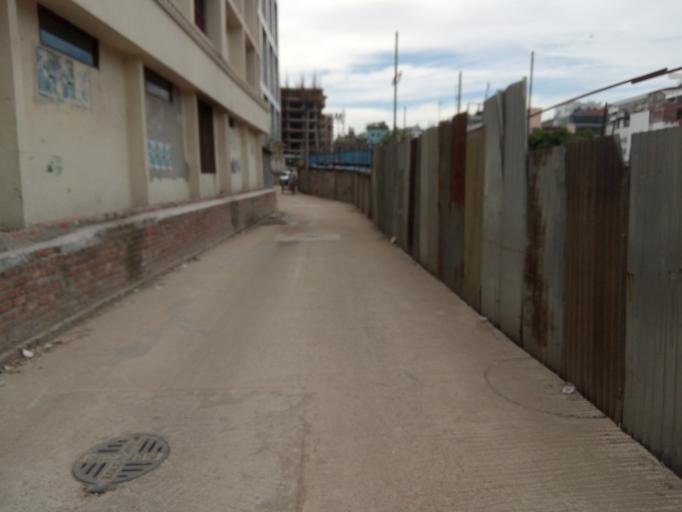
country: BD
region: Dhaka
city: Azimpur
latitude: 23.7491
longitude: 90.3928
